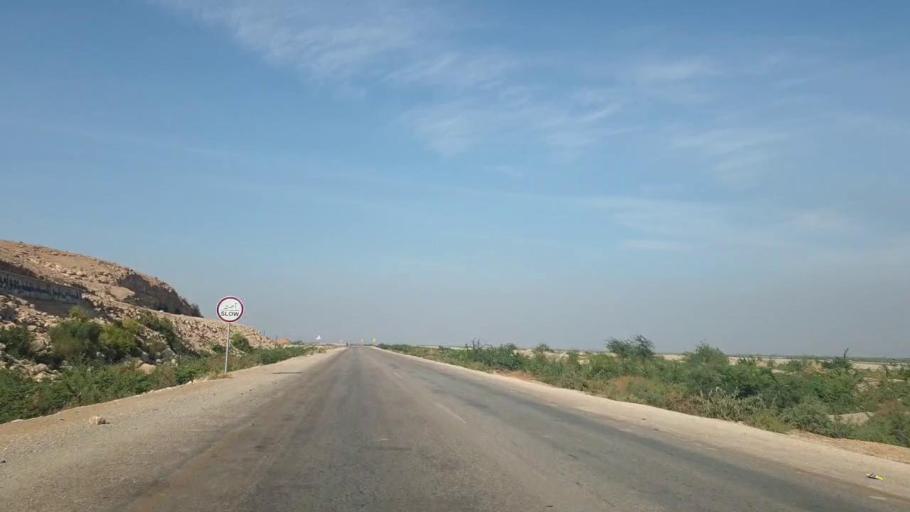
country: PK
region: Sindh
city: Sehwan
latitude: 26.3684
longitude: 67.8739
